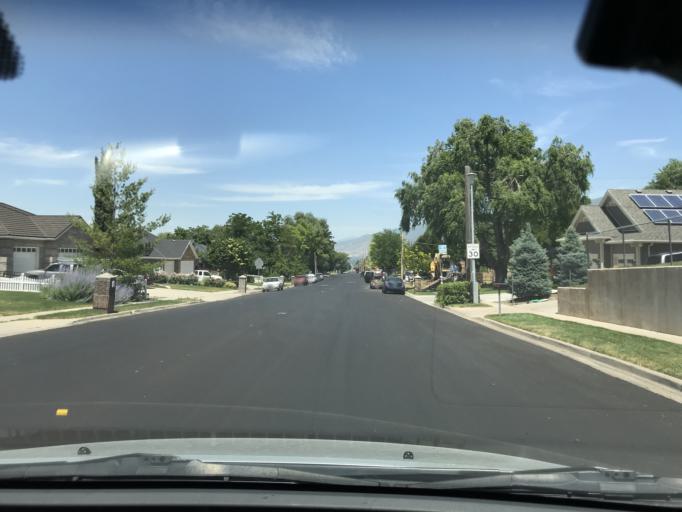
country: US
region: Utah
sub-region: Davis County
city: Woods Cross
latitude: 40.8621
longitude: -111.8857
